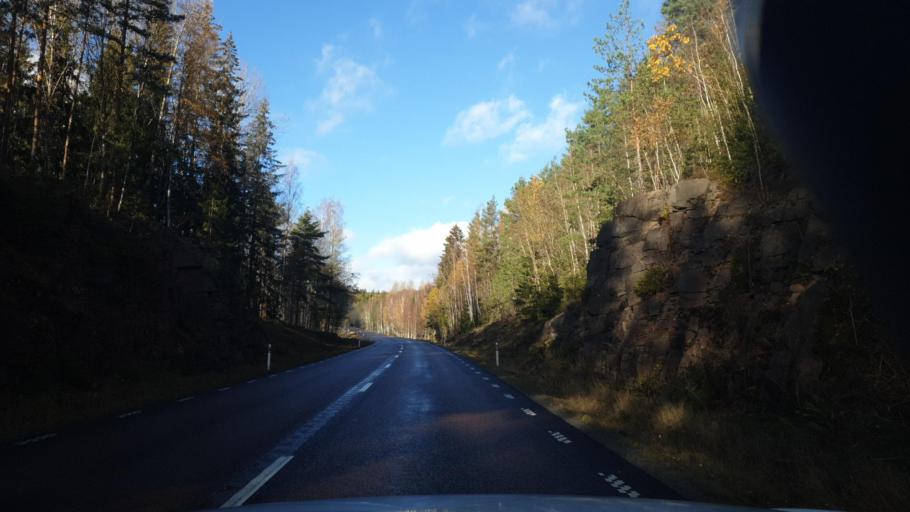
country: SE
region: Vaermland
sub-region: Arvika Kommun
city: Arvika
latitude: 59.5773
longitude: 12.7090
